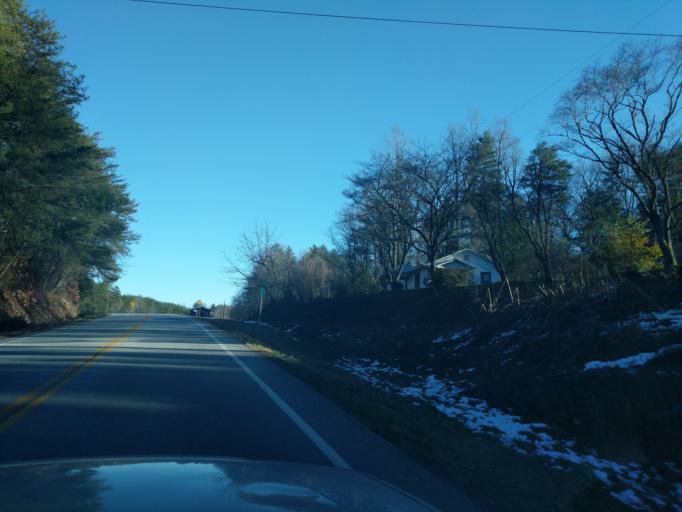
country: US
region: Georgia
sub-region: Rabun County
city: Clayton
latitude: 34.8341
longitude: -83.3275
